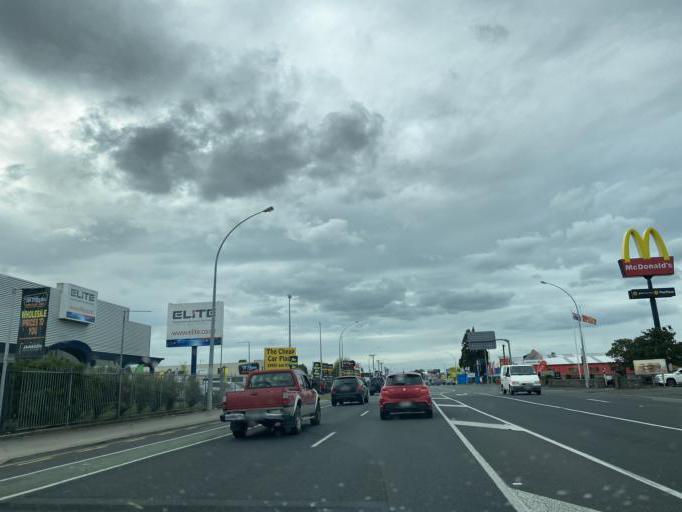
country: NZ
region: Waikato
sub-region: Hamilton City
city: Hamilton
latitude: -37.7944
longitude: 175.2605
